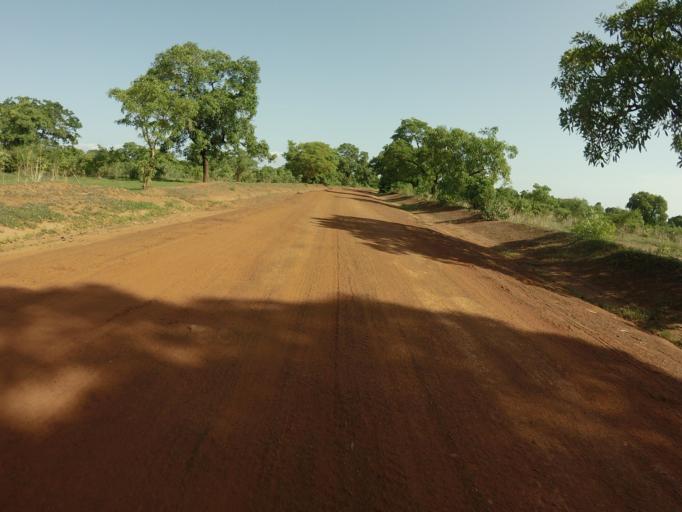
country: GH
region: Upper East
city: Bawku
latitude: 10.7406
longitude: -0.2004
